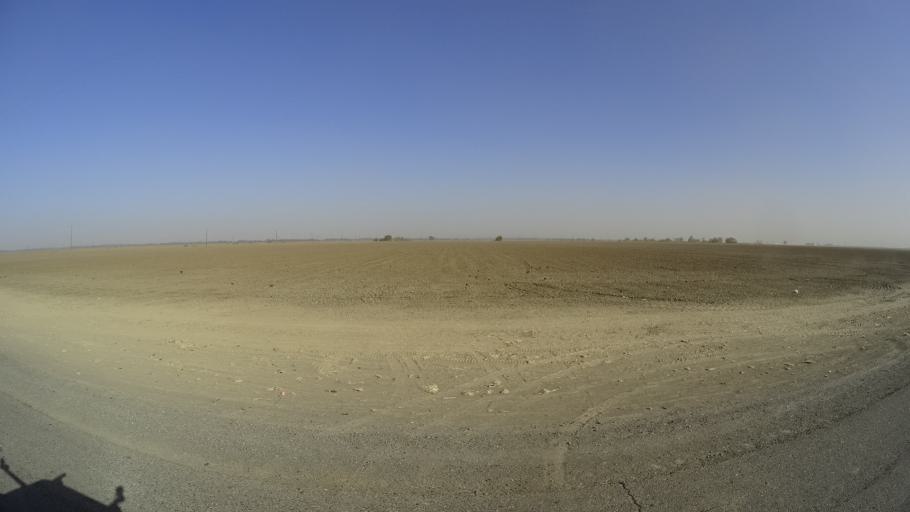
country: US
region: California
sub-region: Yolo County
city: Woodland
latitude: 38.7550
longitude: -121.7292
